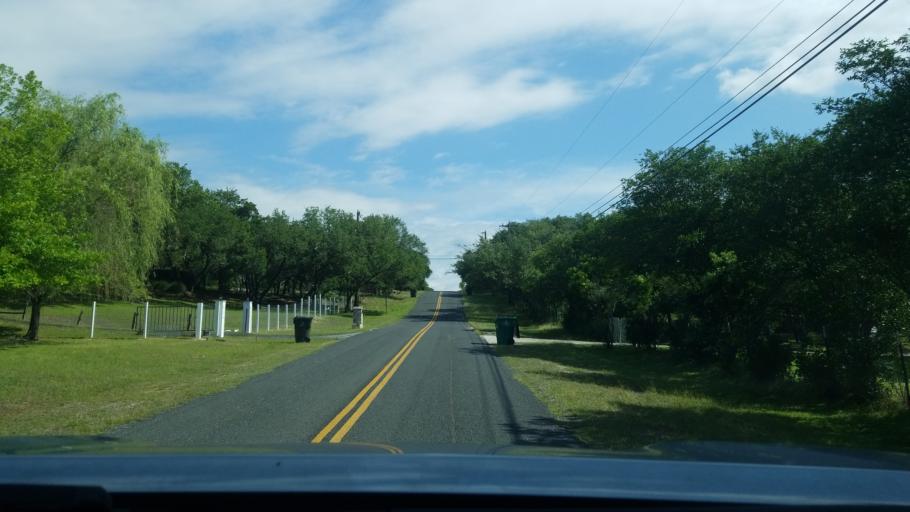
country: US
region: Texas
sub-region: Comal County
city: Bulverde
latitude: 29.7615
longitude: -98.4421
